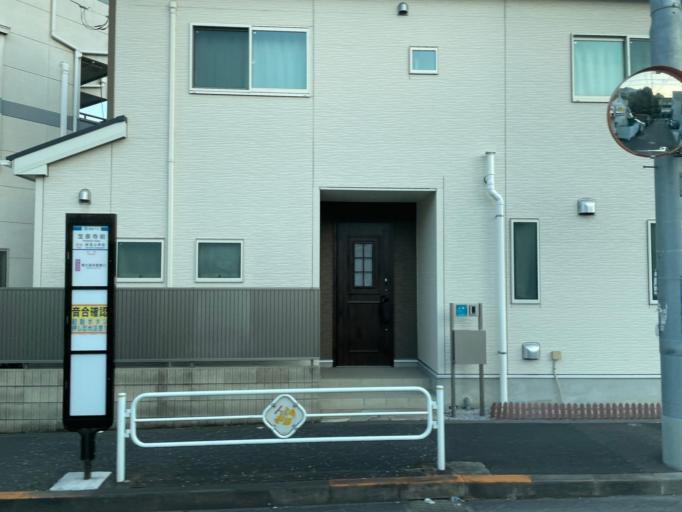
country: JP
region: Tokyo
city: Tanashicho
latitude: 35.7675
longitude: 139.5432
